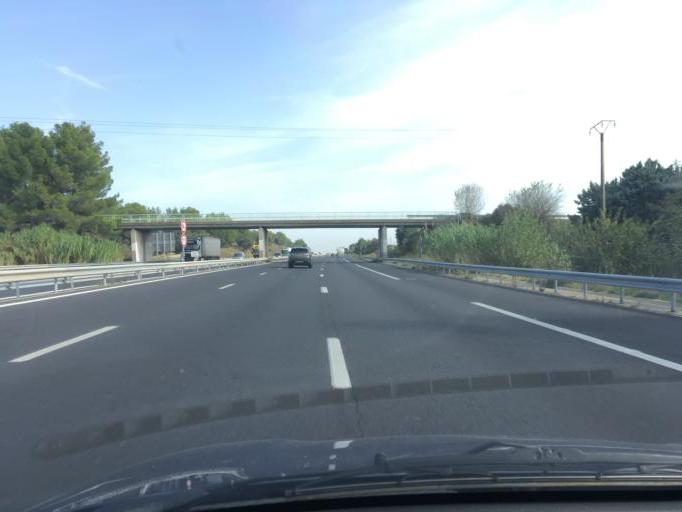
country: FR
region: Languedoc-Roussillon
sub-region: Departement du Gard
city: Saint-Gervasy
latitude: 43.8804
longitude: 4.4670
